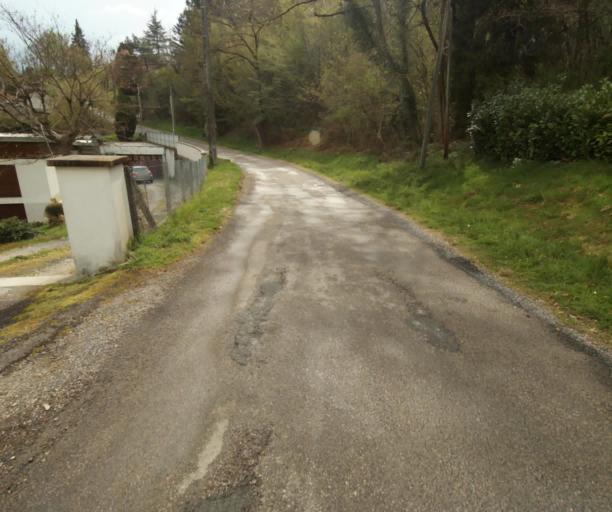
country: FR
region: Limousin
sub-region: Departement de la Correze
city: Tulle
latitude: 45.2718
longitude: 1.7558
